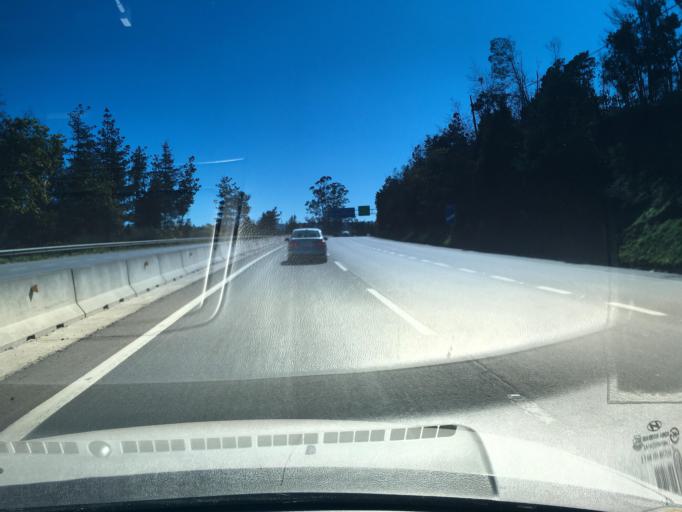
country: CL
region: Valparaiso
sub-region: Provincia de Valparaiso
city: Vina del Mar
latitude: -33.1413
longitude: -71.5624
